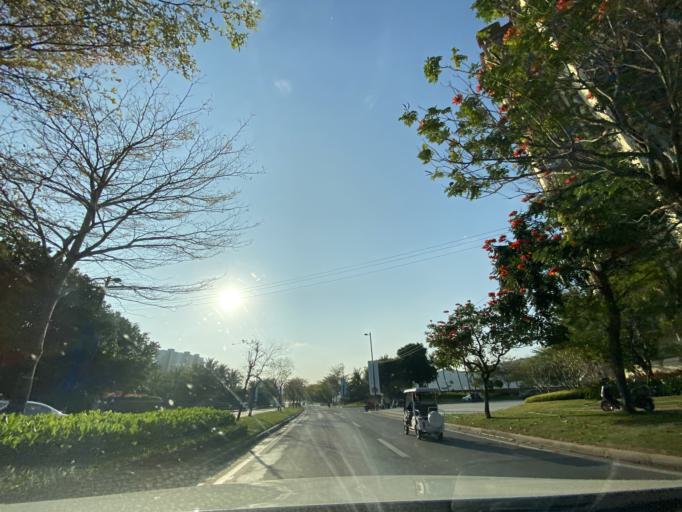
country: CN
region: Hainan
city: Xincun
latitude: 18.4244
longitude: 109.9315
